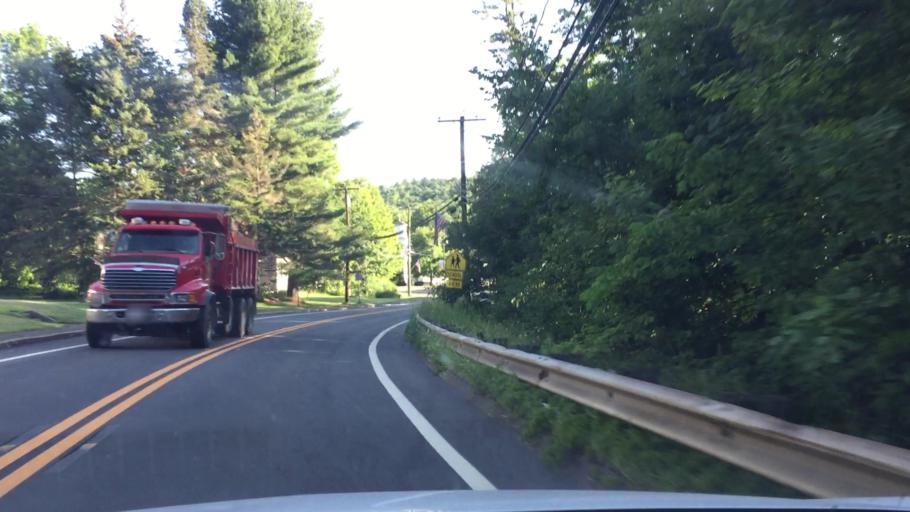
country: US
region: Massachusetts
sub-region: Berkshire County
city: Becket
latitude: 42.3296
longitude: -73.0838
